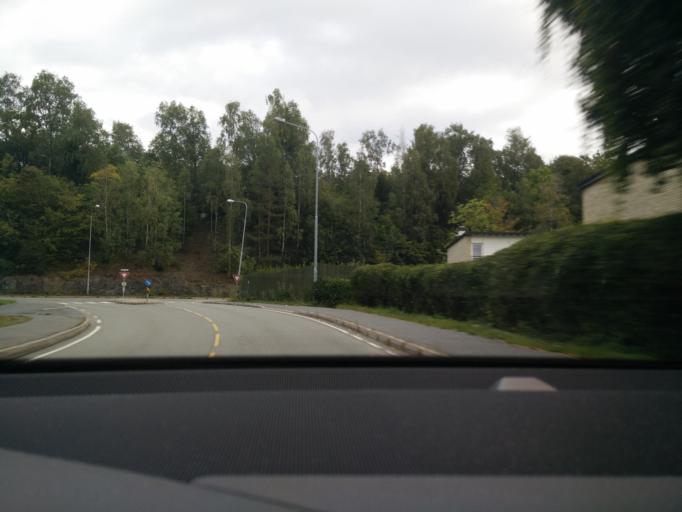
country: NO
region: Akershus
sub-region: Baerum
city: Lysaker
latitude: 59.9372
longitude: 10.6078
